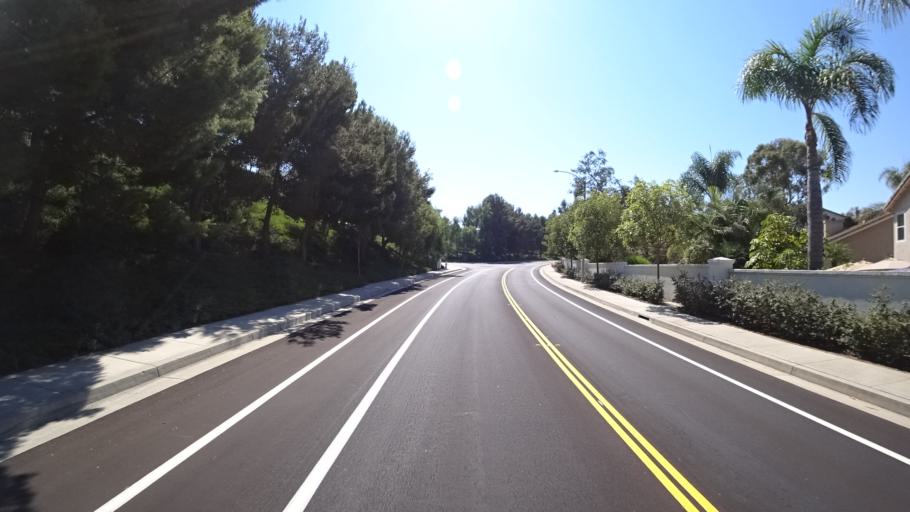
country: US
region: California
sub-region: Orange County
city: San Clemente
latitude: 33.4722
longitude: -117.6210
